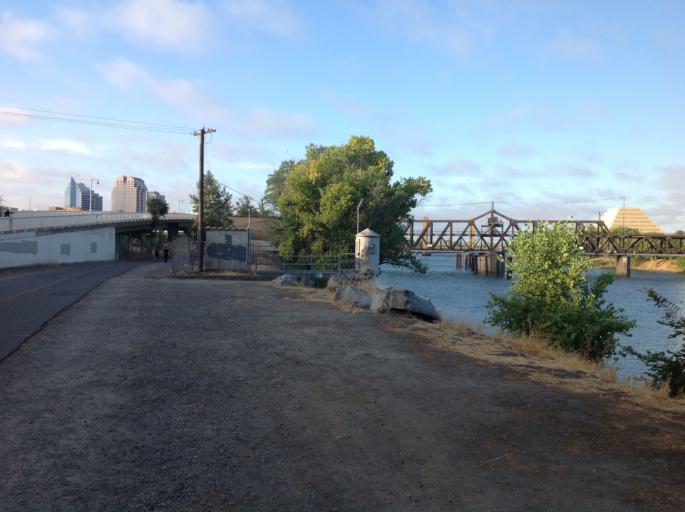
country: US
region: California
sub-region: Sacramento County
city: Sacramento
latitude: 38.5891
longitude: -121.5050
